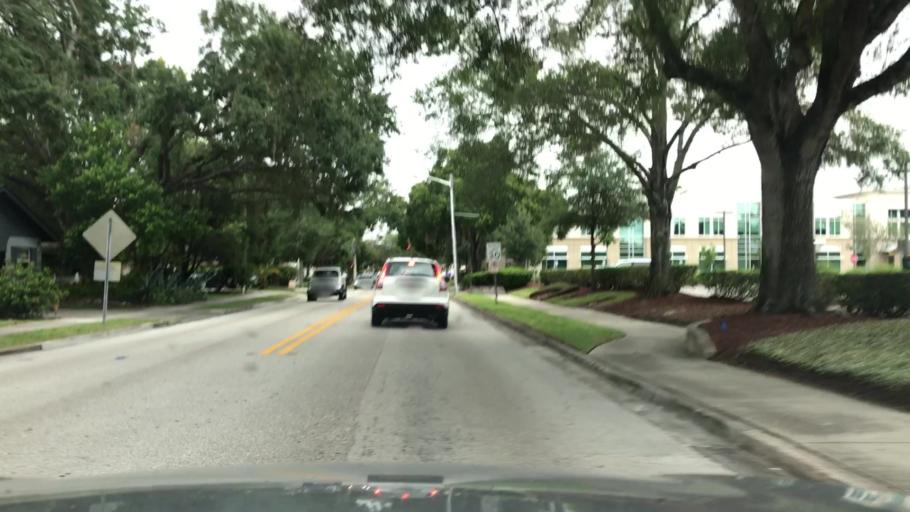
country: US
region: Florida
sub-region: Orange County
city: Winter Park
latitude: 28.5949
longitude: -81.3279
